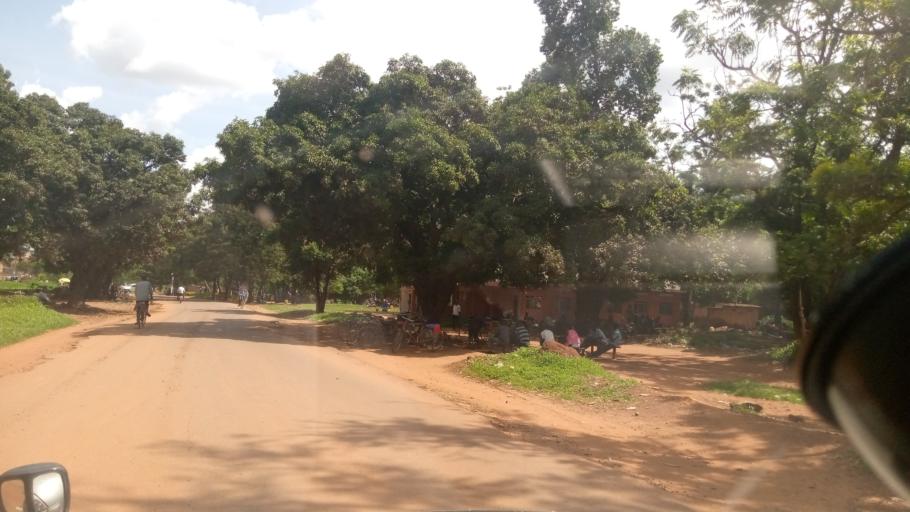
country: UG
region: Northern Region
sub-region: Lira District
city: Lira
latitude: 2.2498
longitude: 32.8989
